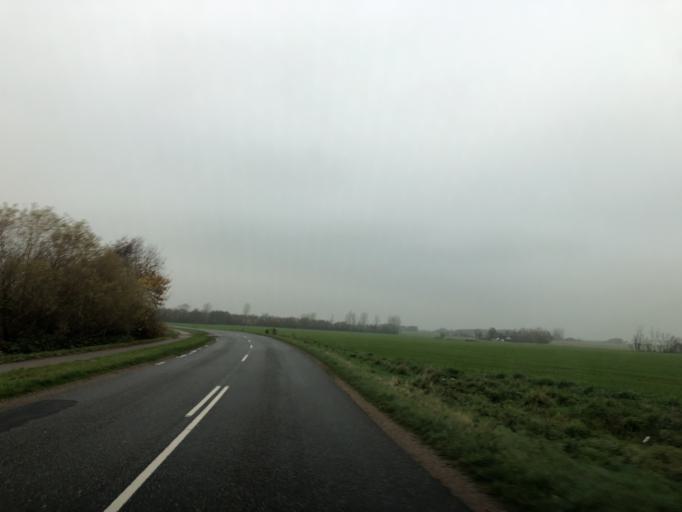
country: DK
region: Central Jutland
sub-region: Herning Kommune
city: Vildbjerg
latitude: 56.2086
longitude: 8.7563
